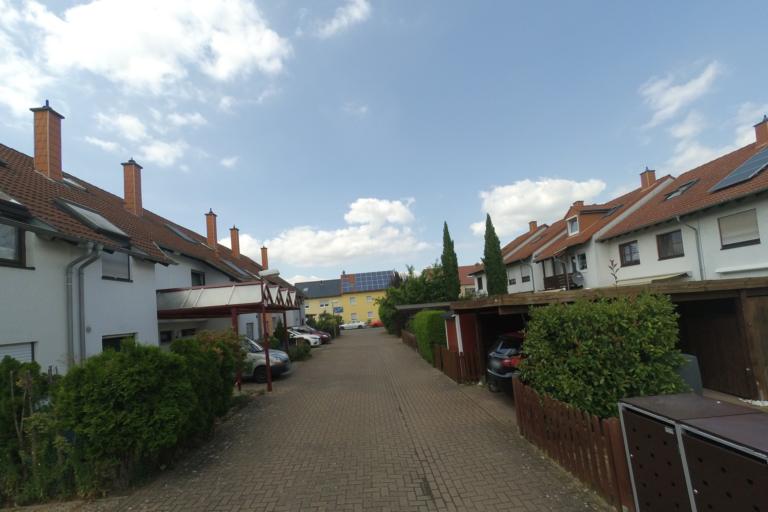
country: DE
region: Rheinland-Pfalz
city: Frankenthal
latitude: 49.5140
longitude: 8.4011
